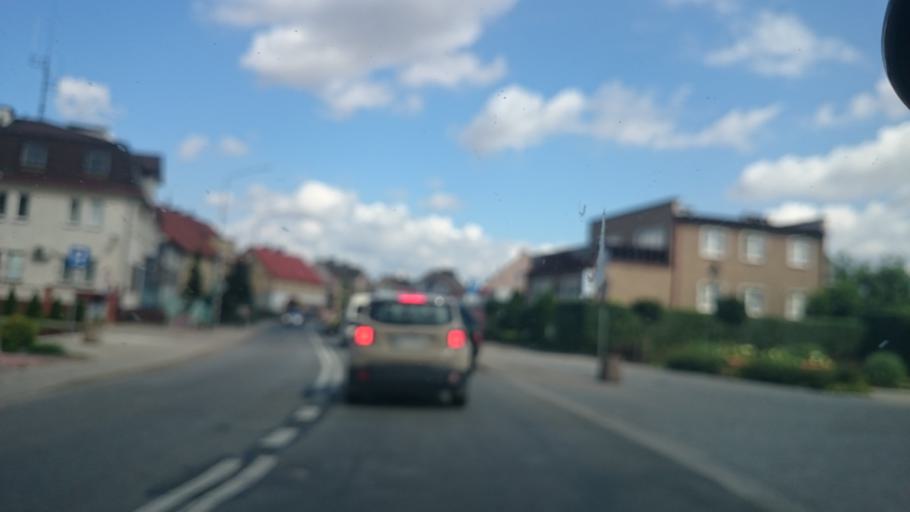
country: PL
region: Lower Silesian Voivodeship
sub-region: Powiat zabkowicki
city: Kamieniec Zabkowicki
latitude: 50.5206
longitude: 16.8732
